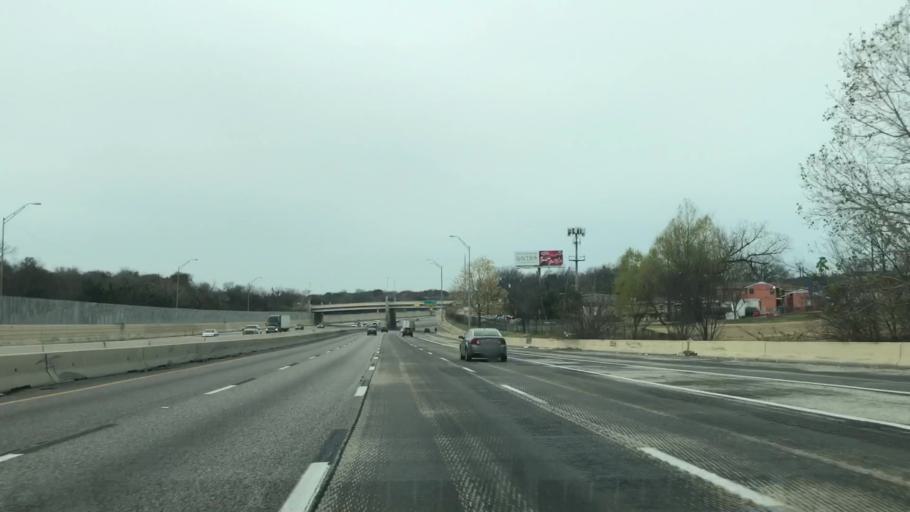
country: US
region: Texas
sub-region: Dallas County
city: Dallas
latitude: 32.7663
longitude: -96.8397
